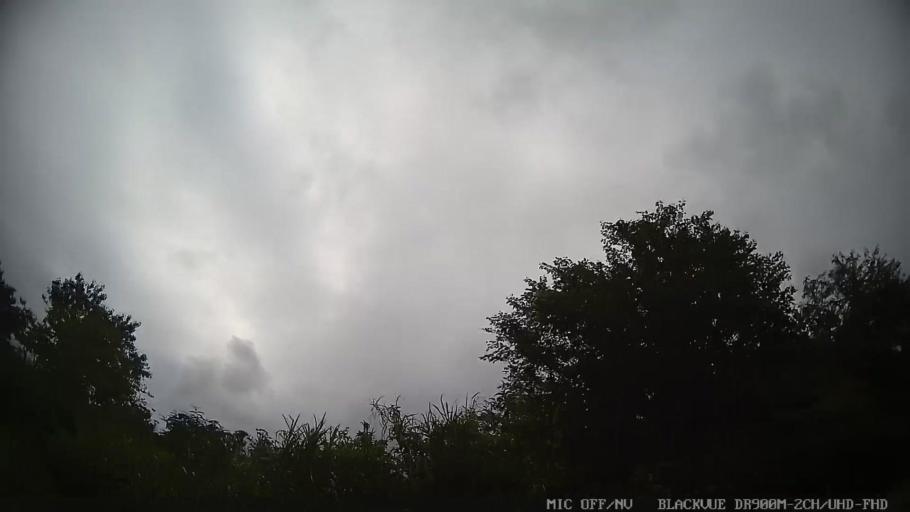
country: BR
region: Sao Paulo
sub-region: Osasco
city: Osasco
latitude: -23.4786
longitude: -46.7327
